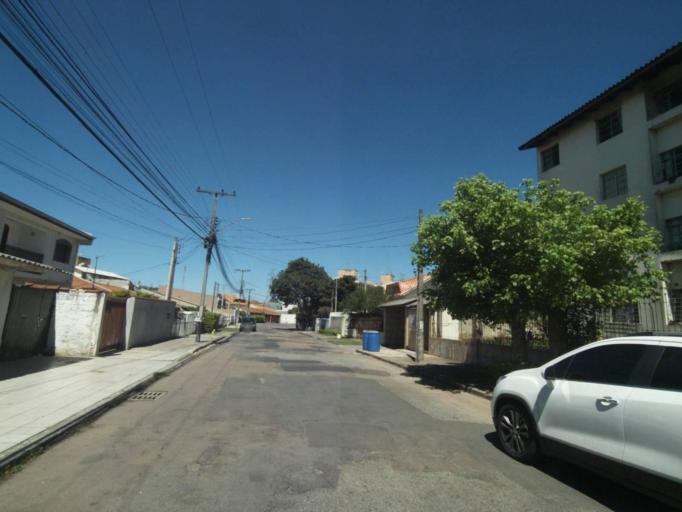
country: BR
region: Parana
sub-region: Curitiba
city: Curitiba
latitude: -25.4766
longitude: -49.3384
